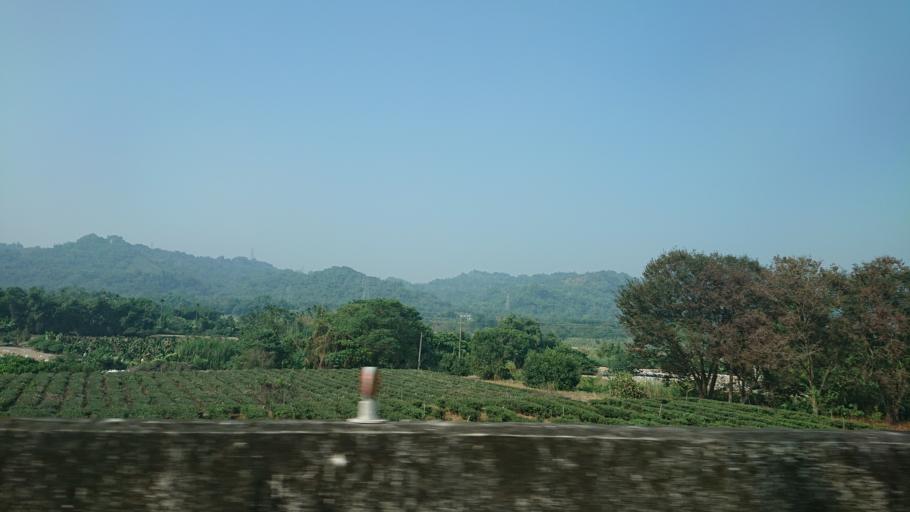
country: TW
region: Taiwan
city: Lugu
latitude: 23.7070
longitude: 120.6638
